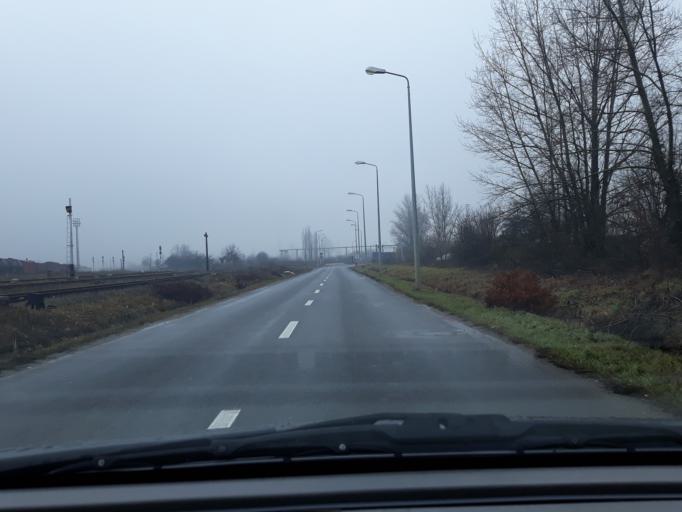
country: RO
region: Bihor
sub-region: Comuna Sanmartin
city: Sanmartin
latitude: 47.0385
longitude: 21.9652
